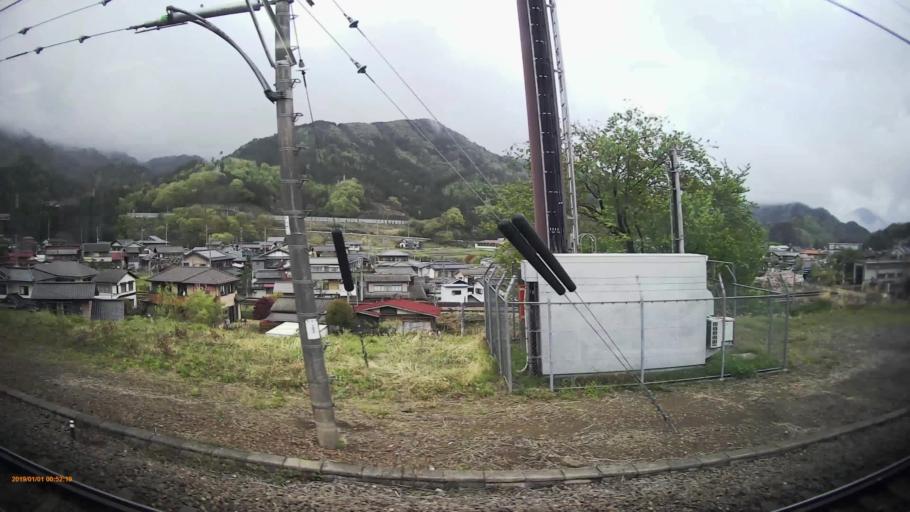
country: JP
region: Yamanashi
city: Otsuki
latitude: 35.5946
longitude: 138.8813
